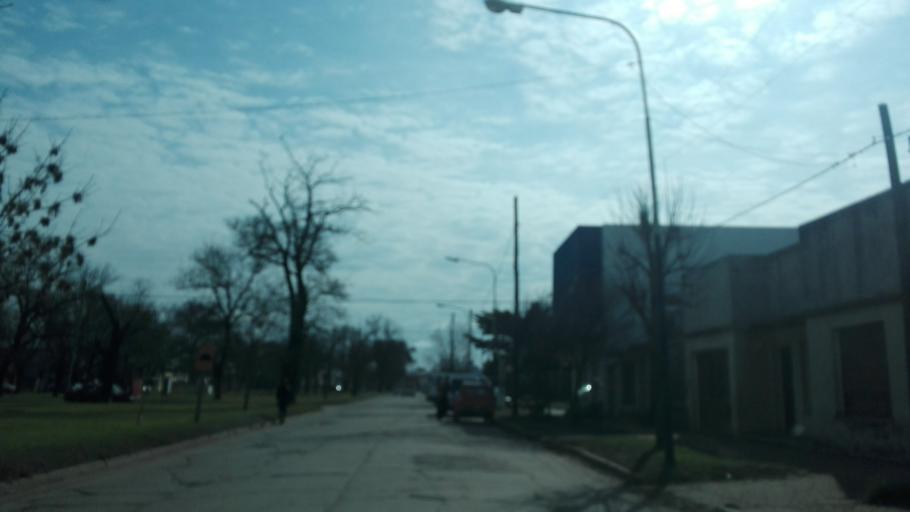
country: AR
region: Buenos Aires
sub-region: Partido de Chascomus
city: Chascomus
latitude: -35.5700
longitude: -58.0096
